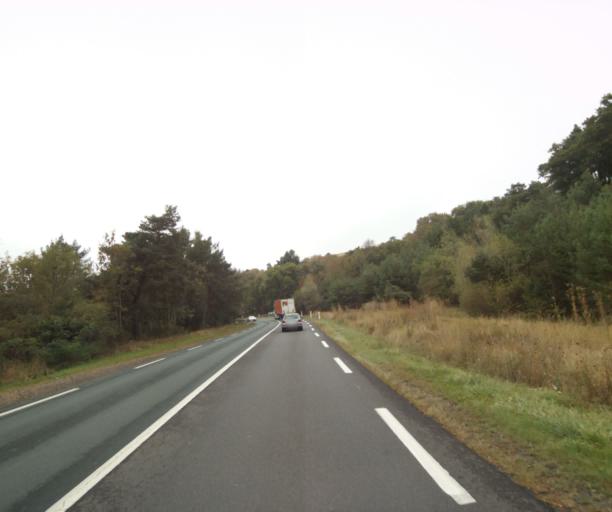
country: FR
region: Auvergne
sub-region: Departement du Puy-de-Dome
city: Ceyrat
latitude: 45.7084
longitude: 3.0595
